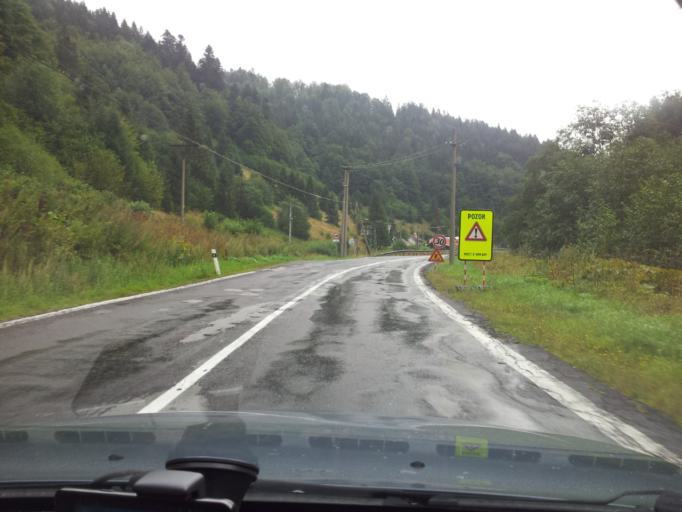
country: SK
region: Banskobystricky
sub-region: Okres Banska Bystrica
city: Brezno
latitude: 48.8921
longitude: 19.6915
